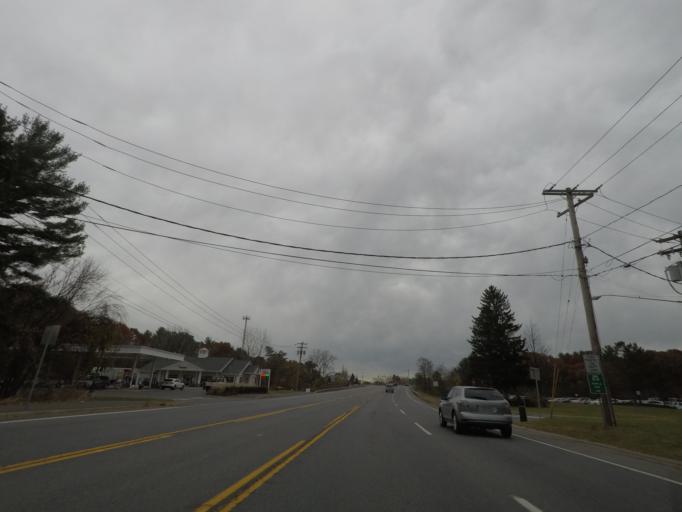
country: US
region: New York
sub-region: Schenectady County
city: Niskayuna
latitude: 42.8193
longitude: -73.7716
